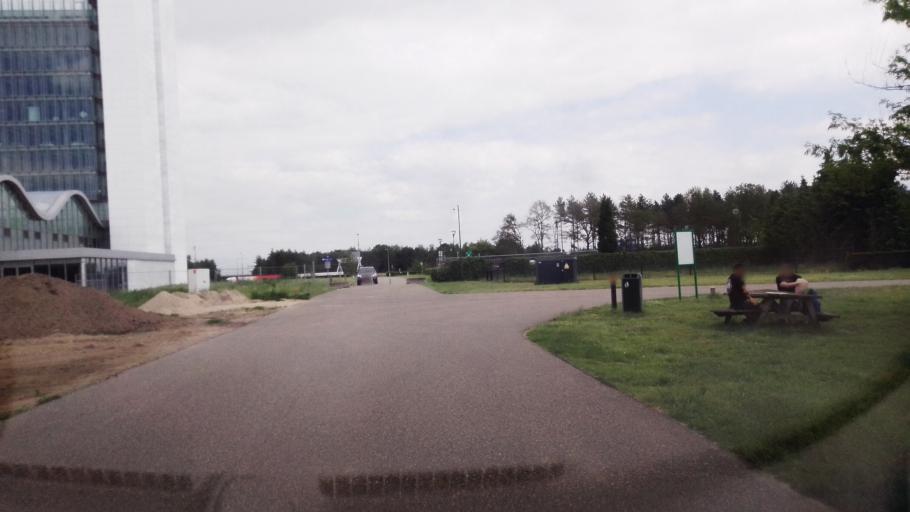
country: NL
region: Limburg
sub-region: Gemeente Venlo
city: Venlo
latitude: 51.4032
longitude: 6.1237
